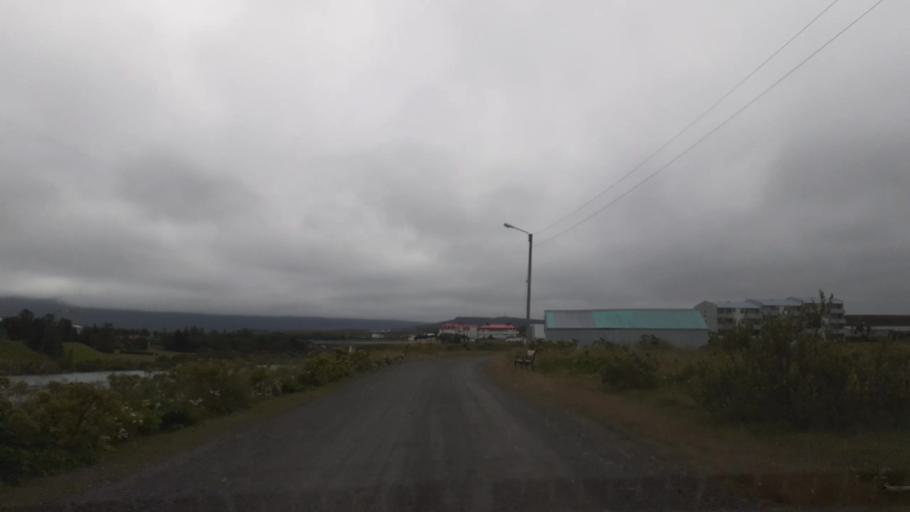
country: IS
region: Northwest
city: Saudarkrokur
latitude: 65.6590
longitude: -20.2919
